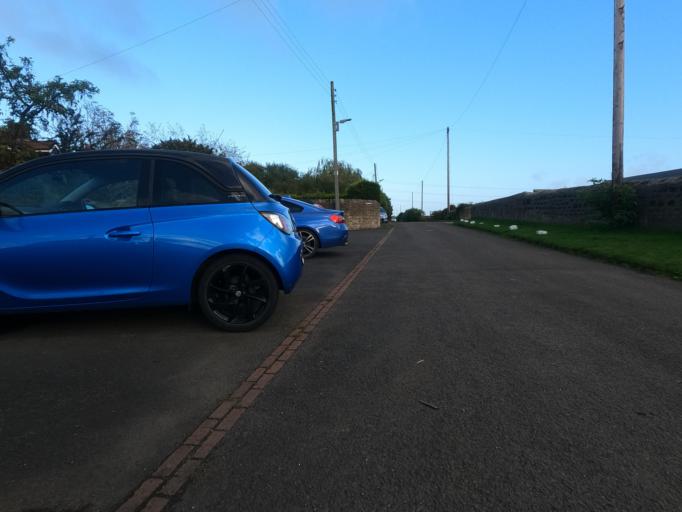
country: GB
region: England
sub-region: Northumberland
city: Seghill
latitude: 55.0692
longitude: -1.5428
